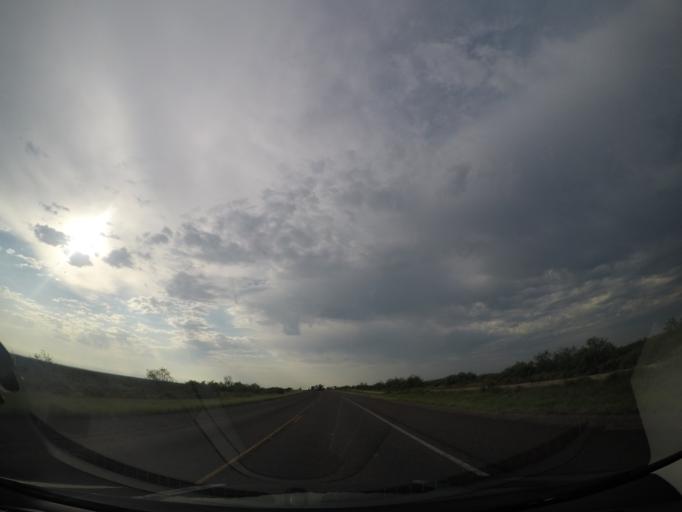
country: US
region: Texas
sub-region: Terrell County
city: Sanderson
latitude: 29.9492
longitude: -101.9921
